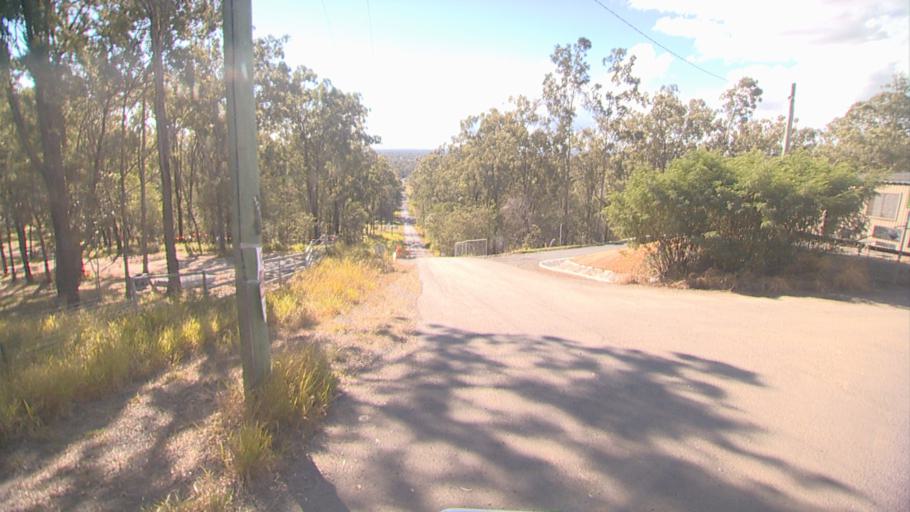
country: AU
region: Queensland
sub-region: Logan
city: Chambers Flat
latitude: -27.8121
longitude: 153.0815
